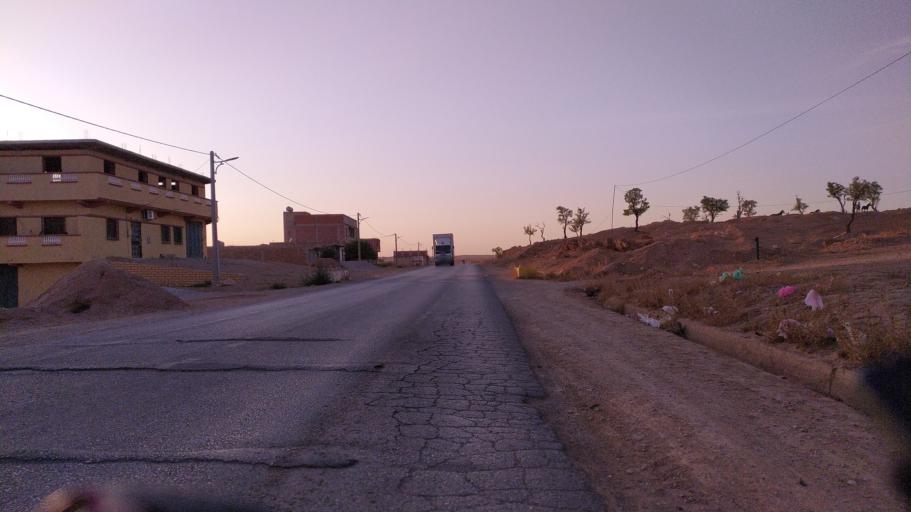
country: DZ
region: Tiaret
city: Frenda
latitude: 34.8985
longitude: 1.2465
